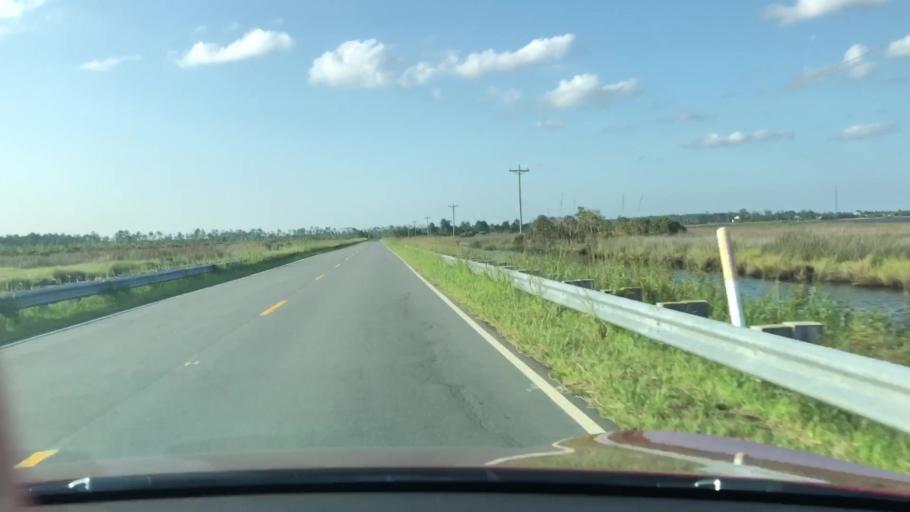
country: US
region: North Carolina
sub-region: Dare County
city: Wanchese
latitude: 35.6845
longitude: -75.7804
